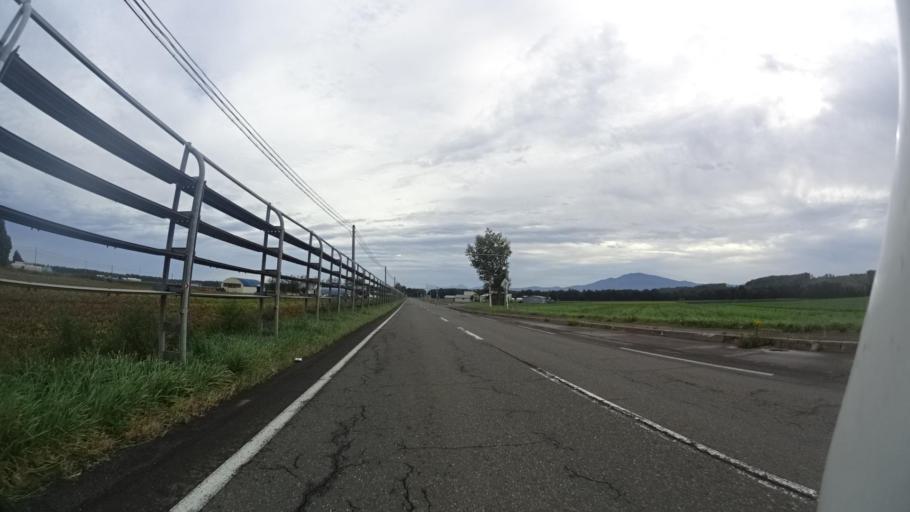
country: JP
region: Hokkaido
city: Abashiri
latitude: 43.8570
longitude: 144.6084
